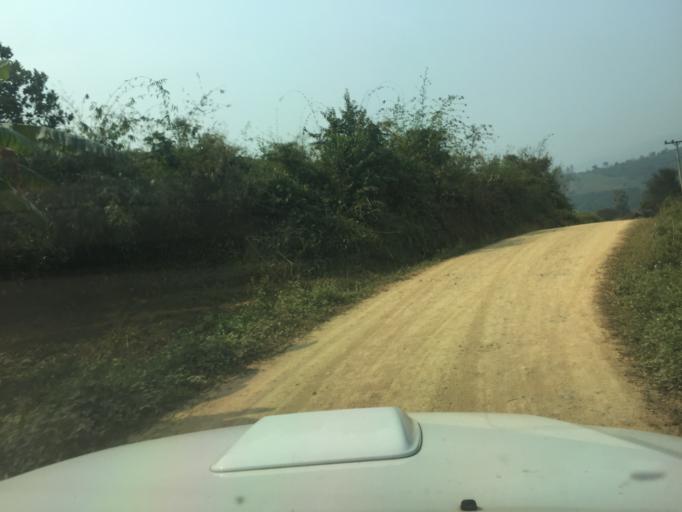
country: TH
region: Phayao
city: Phu Sang
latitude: 19.6220
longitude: 100.5388
